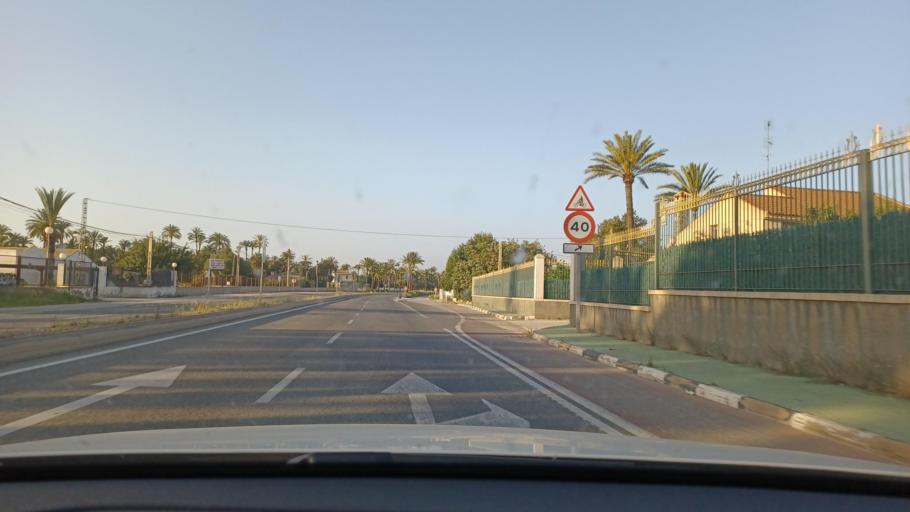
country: ES
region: Valencia
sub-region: Provincia de Alicante
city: Elche
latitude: 38.2482
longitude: -0.6980
